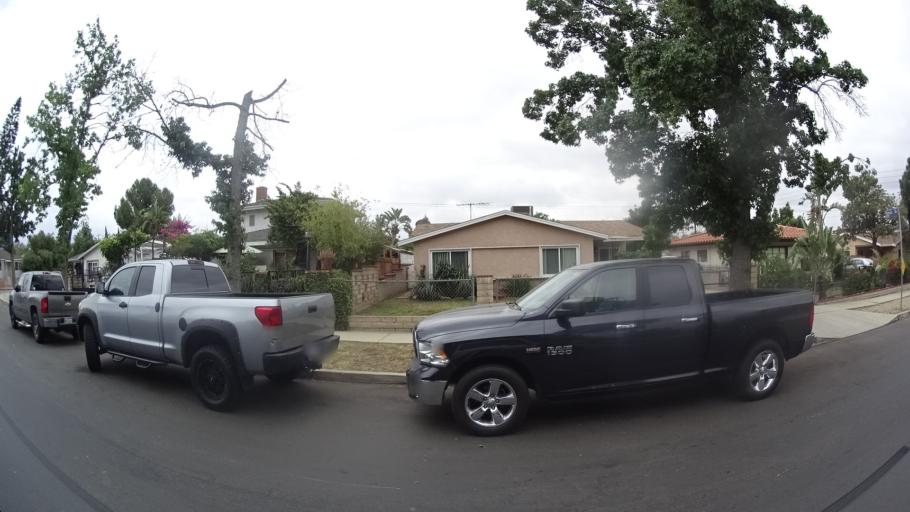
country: US
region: California
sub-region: Los Angeles County
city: San Fernando
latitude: 34.2795
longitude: -118.4523
